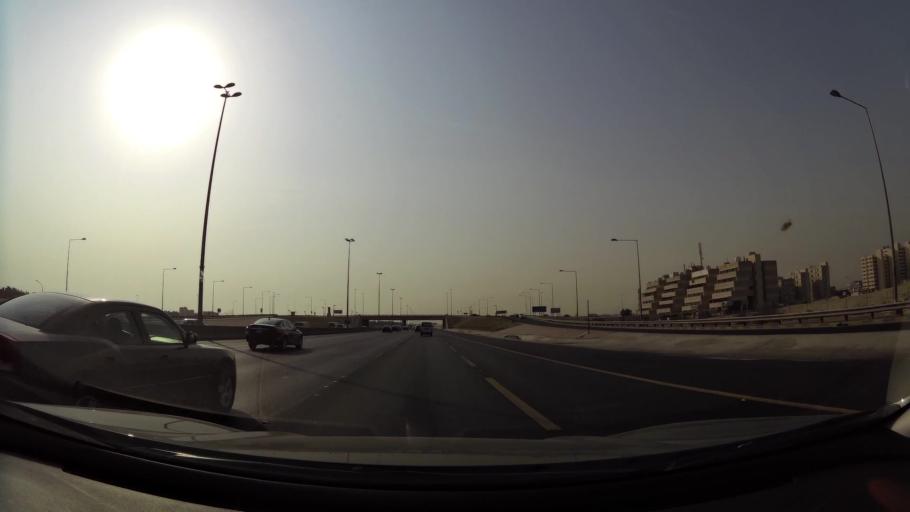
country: KW
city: Al Funaytis
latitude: 29.2514
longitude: 48.0907
